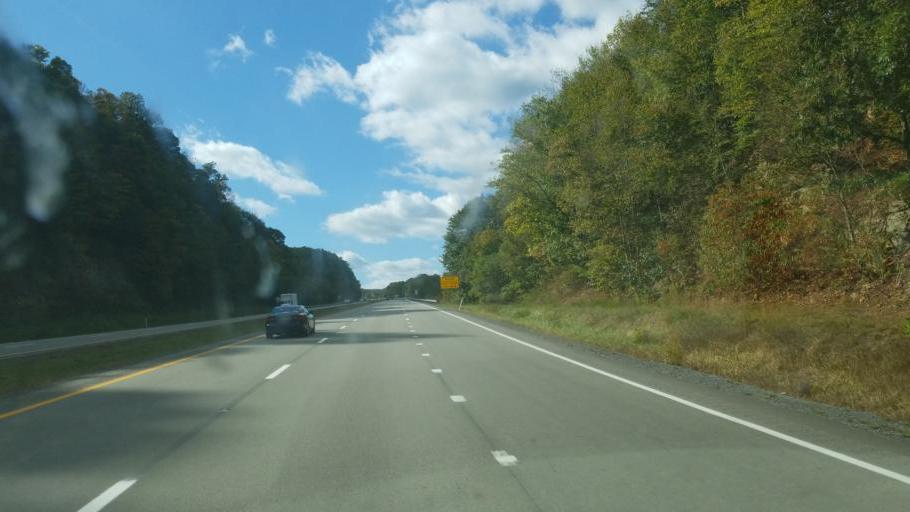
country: US
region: West Virginia
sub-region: Monongalia County
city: Cheat Lake
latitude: 39.6508
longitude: -79.7241
